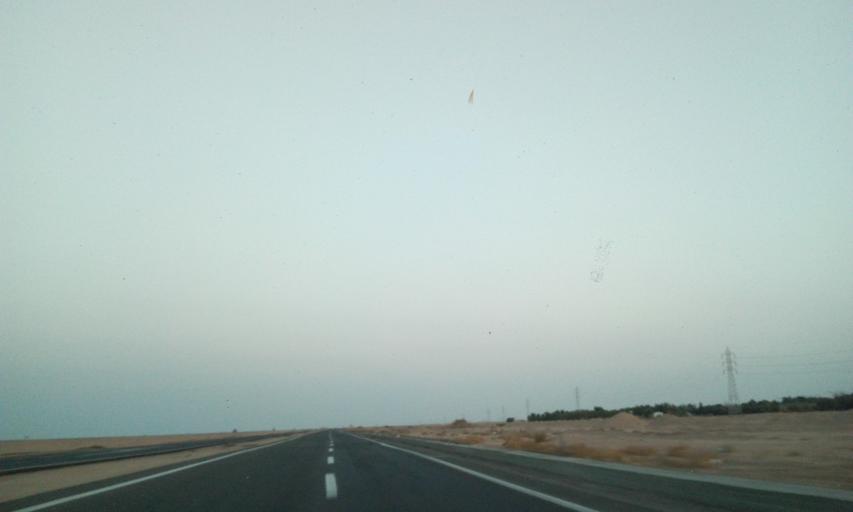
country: EG
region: Red Sea
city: El Gouna
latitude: 27.3613
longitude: 33.6423
